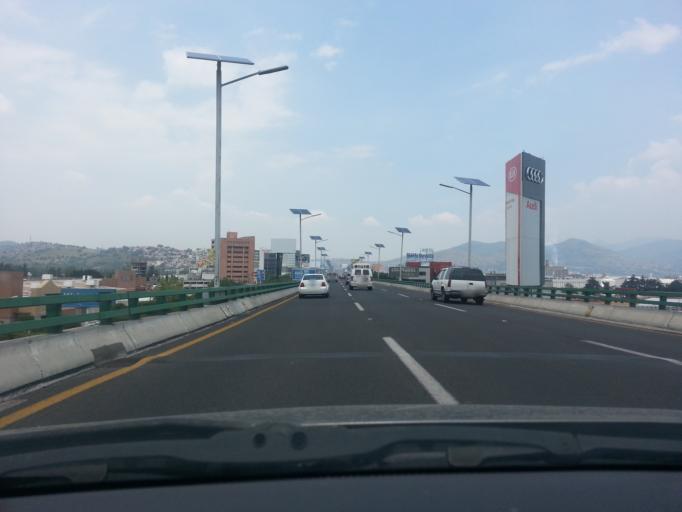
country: MX
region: Mexico
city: Tlalnepantla
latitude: 19.5407
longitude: -99.2140
